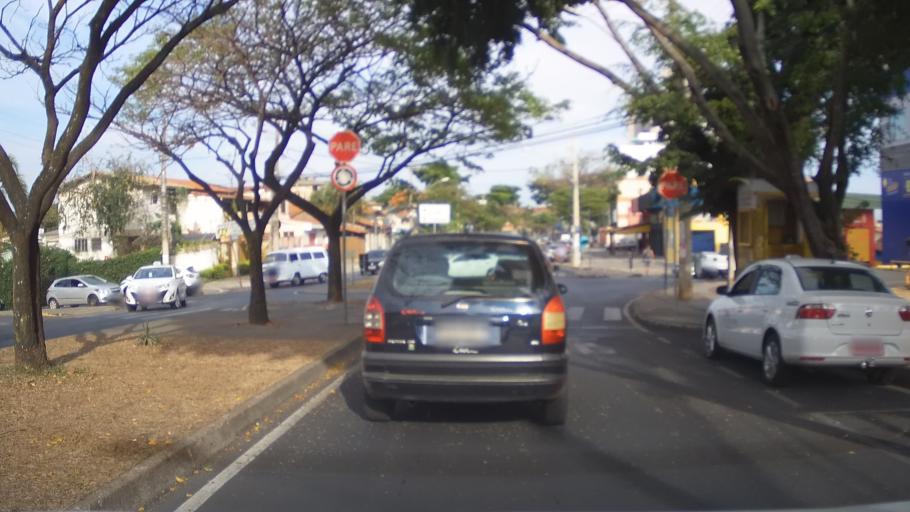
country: BR
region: Minas Gerais
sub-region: Belo Horizonte
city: Belo Horizonte
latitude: -19.8916
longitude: -43.9984
